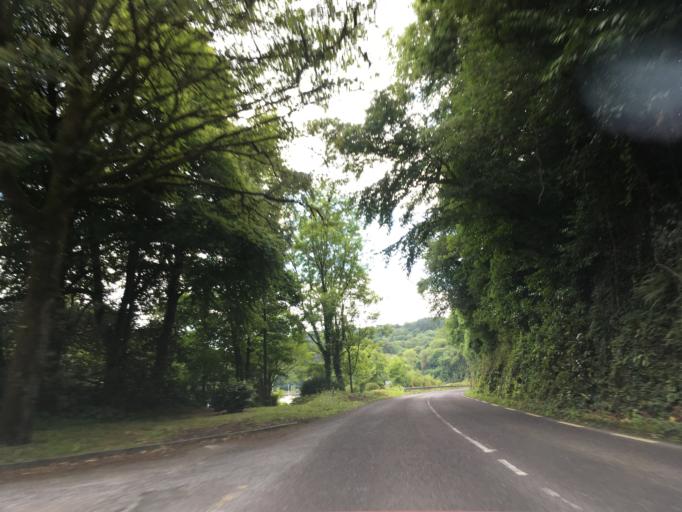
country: IE
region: Munster
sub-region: County Cork
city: Crosshaven
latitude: 51.8035
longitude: -8.3334
